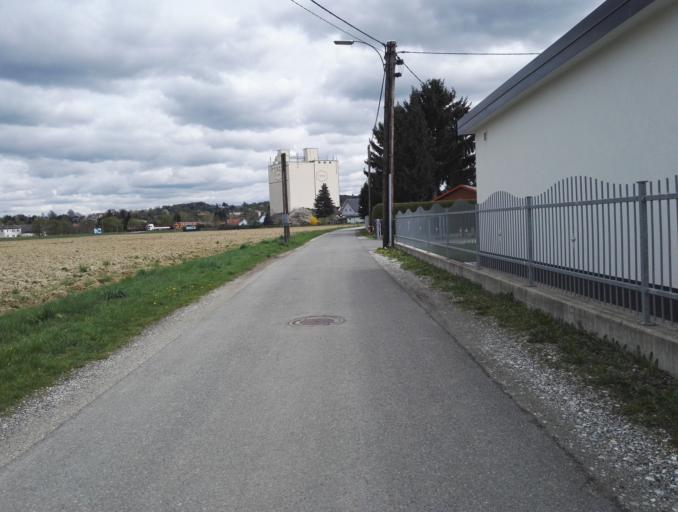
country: AT
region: Styria
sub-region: Politischer Bezirk Graz-Umgebung
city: Raaba
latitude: 47.0316
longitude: 15.4824
